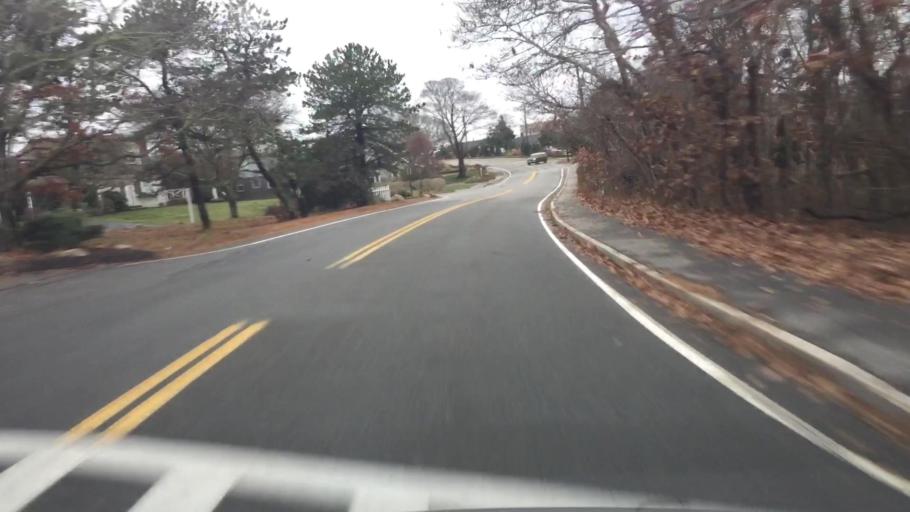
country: US
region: Massachusetts
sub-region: Barnstable County
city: West Falmouth
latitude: 41.6268
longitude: -70.6364
